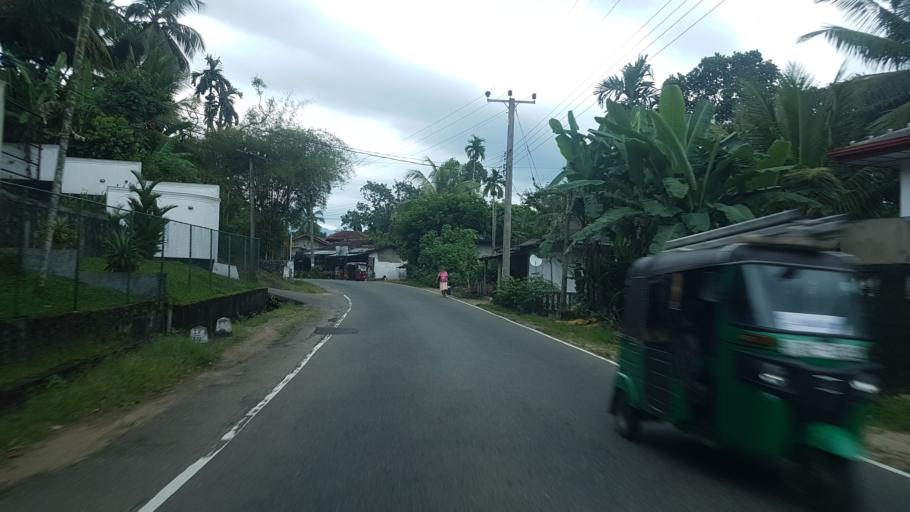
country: LK
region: Western
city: Hanwella Ihala
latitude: 7.0297
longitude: 80.2824
